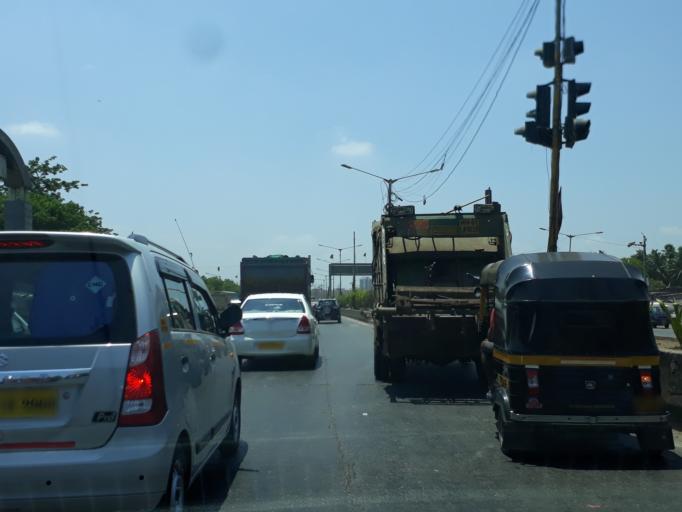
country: IN
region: Maharashtra
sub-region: Mumbai Suburban
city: Mumbai
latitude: 19.0593
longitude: 72.9236
